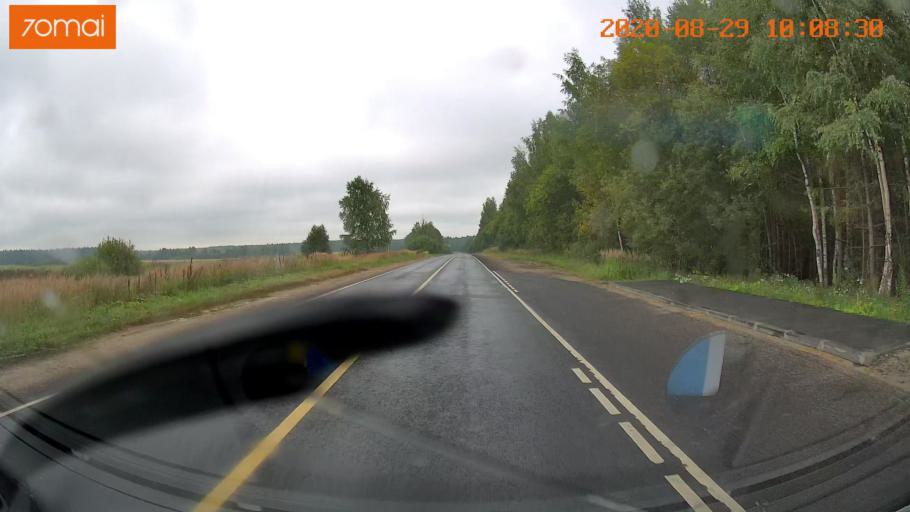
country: RU
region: Ivanovo
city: Kuznechikha
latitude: 57.3758
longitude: 42.5918
